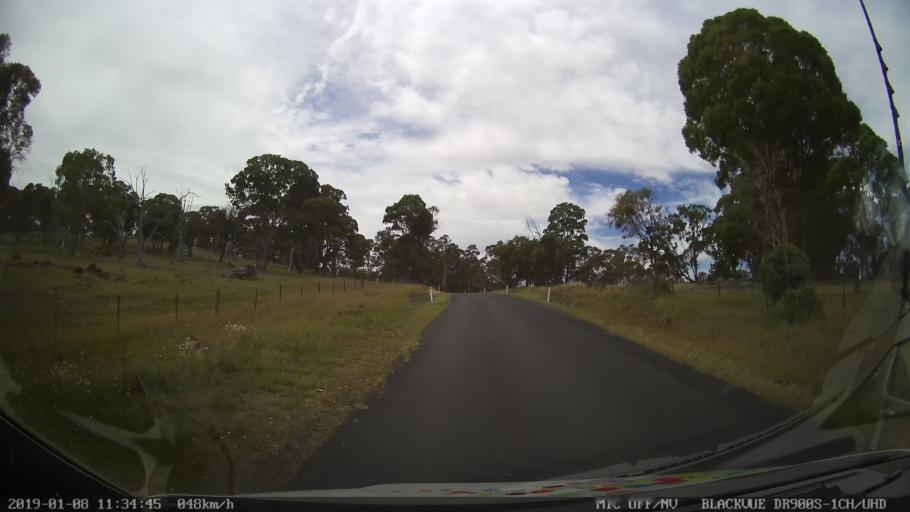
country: AU
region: New South Wales
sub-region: Guyra
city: Guyra
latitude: -30.3318
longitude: 151.5351
